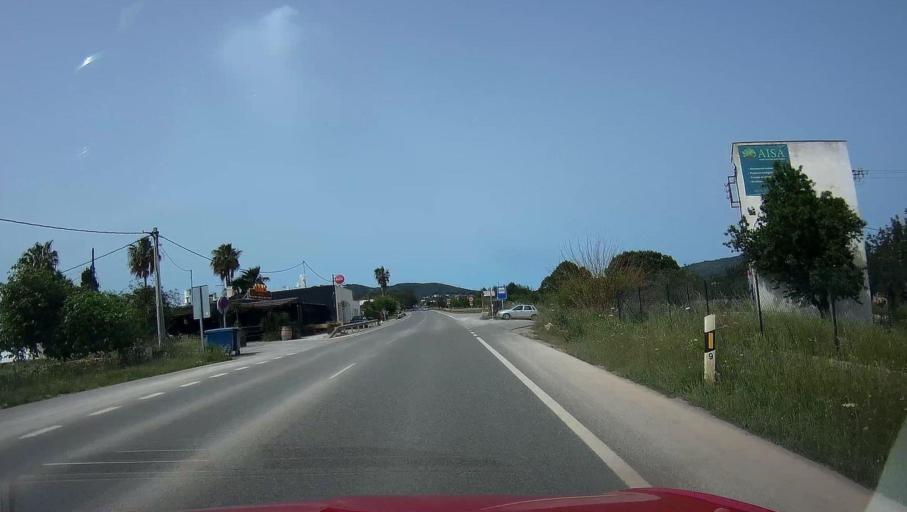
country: ES
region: Balearic Islands
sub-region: Illes Balears
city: Santa Eularia des Riu
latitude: 39.0103
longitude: 1.4879
